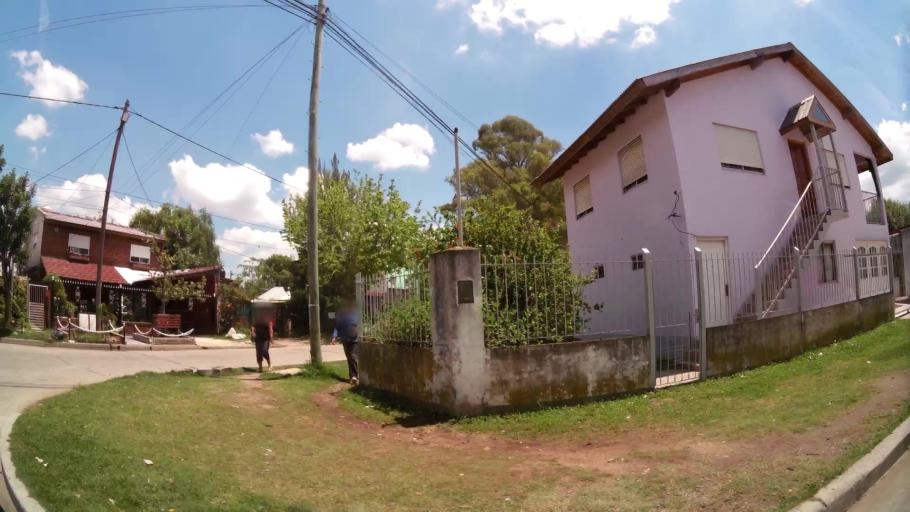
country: AR
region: Buenos Aires
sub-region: Partido de Tigre
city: Tigre
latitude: -34.4055
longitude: -58.6039
